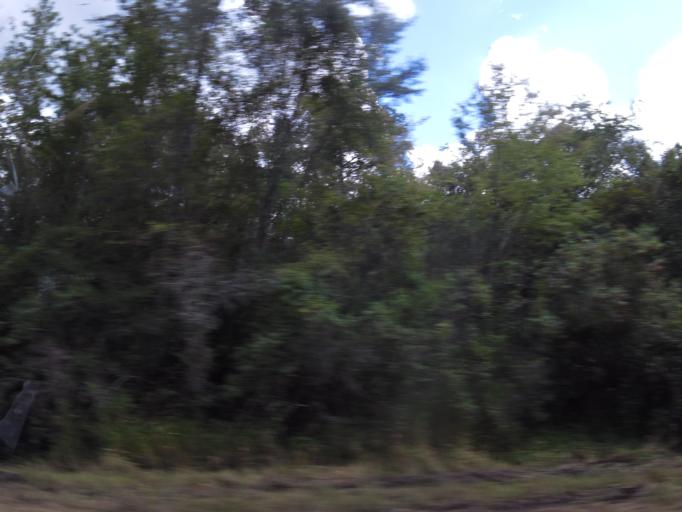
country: US
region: Georgia
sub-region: Charlton County
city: Folkston
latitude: 31.0009
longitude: -82.0267
